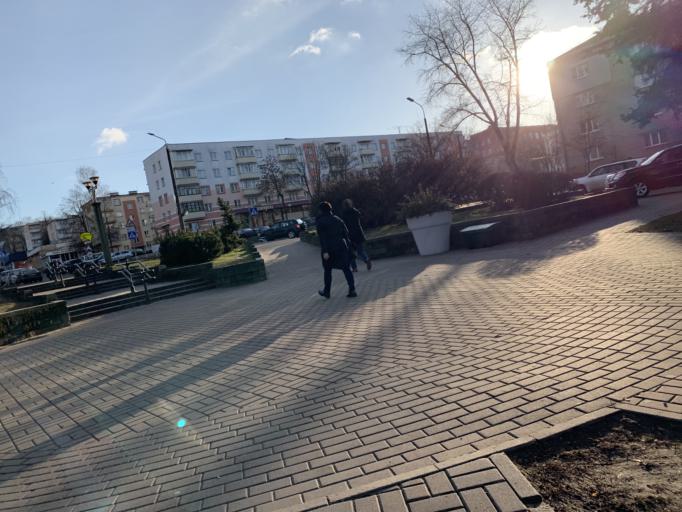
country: BY
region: Minsk
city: Minsk
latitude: 53.9136
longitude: 27.5862
